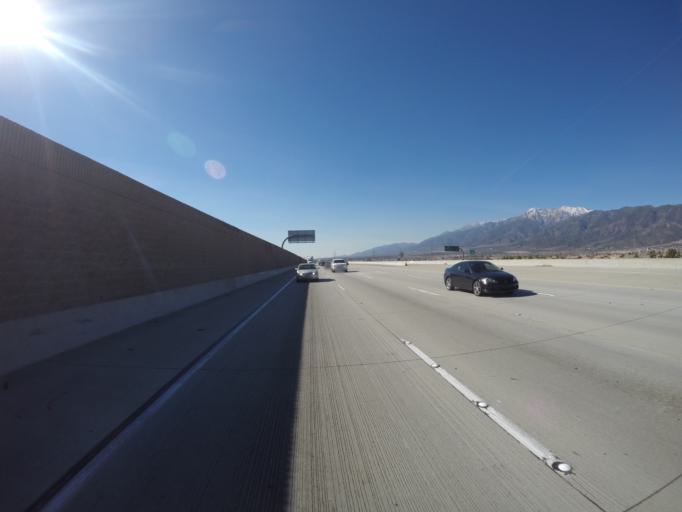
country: US
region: California
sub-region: San Bernardino County
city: Fontana
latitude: 34.1363
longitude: -117.4669
